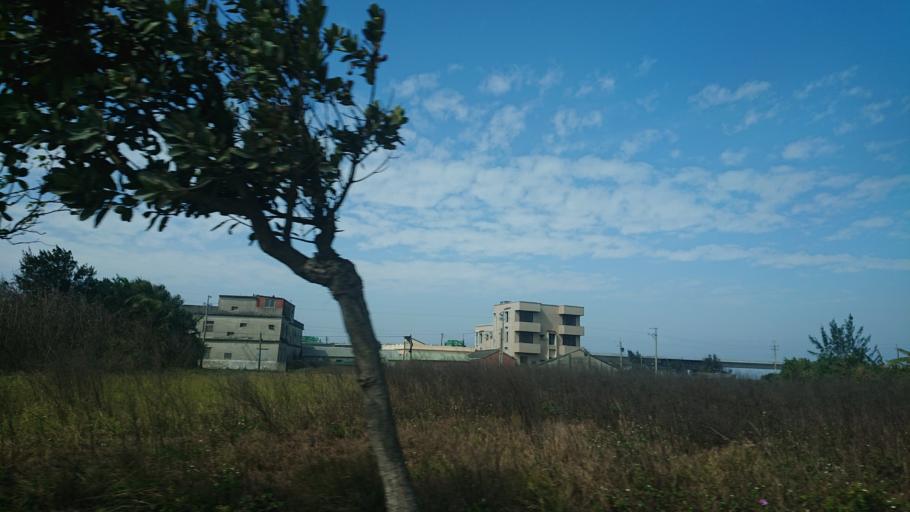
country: TW
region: Taiwan
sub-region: Changhua
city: Chang-hua
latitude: 23.9054
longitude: 120.3081
